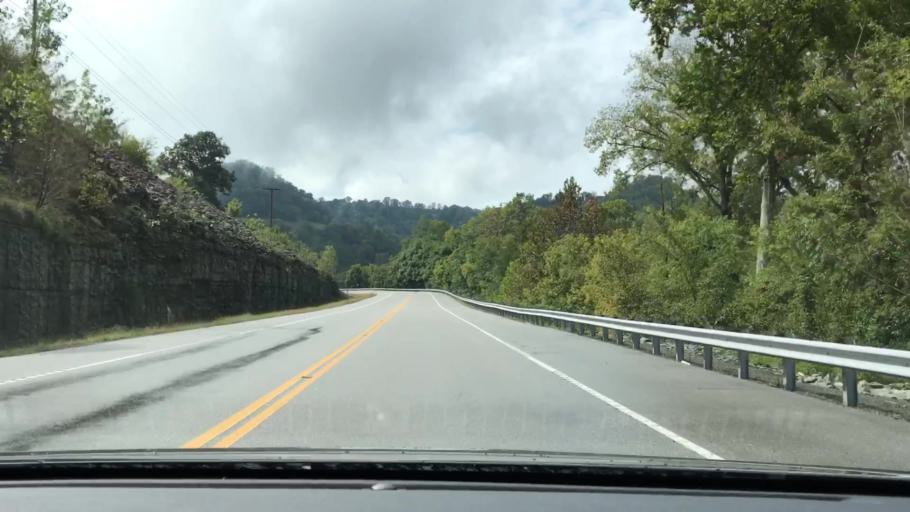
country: US
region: Tennessee
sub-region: Smith County
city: Carthage
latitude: 36.3524
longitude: -85.9607
